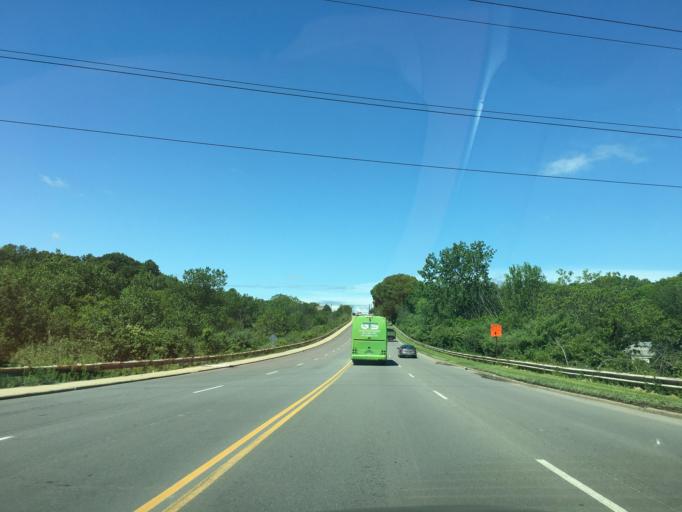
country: US
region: Ohio
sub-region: Cuyahoga County
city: Independence
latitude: 41.3940
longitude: -81.6326
